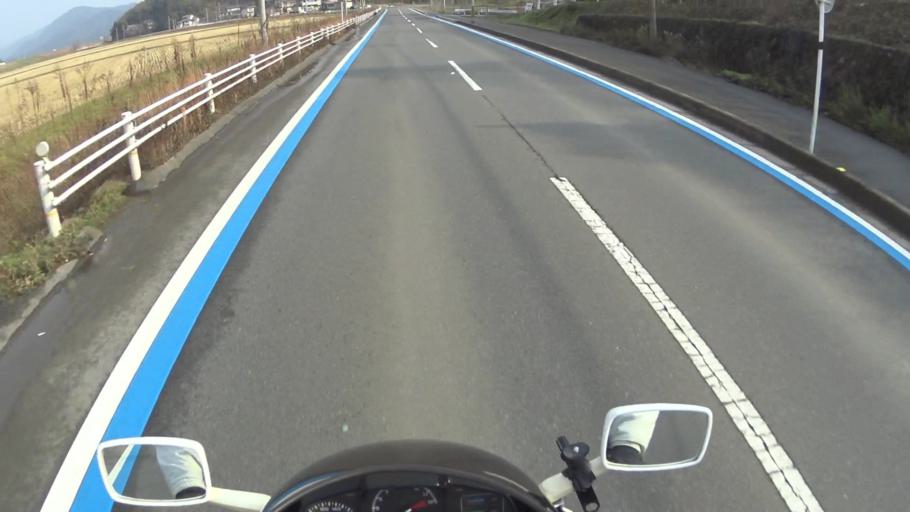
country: JP
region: Kyoto
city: Fukuchiyama
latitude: 35.3741
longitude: 135.1395
